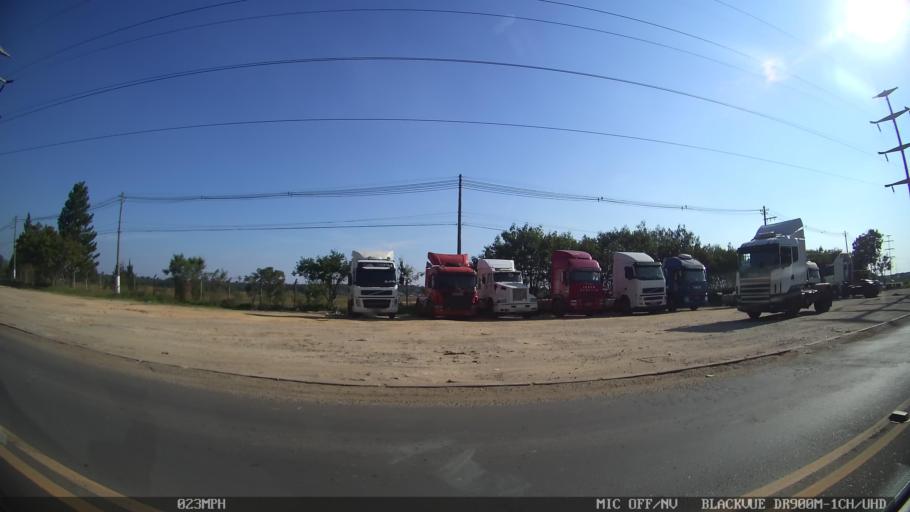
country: BR
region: Sao Paulo
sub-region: Campinas
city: Campinas
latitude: -22.9945
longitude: -47.1319
